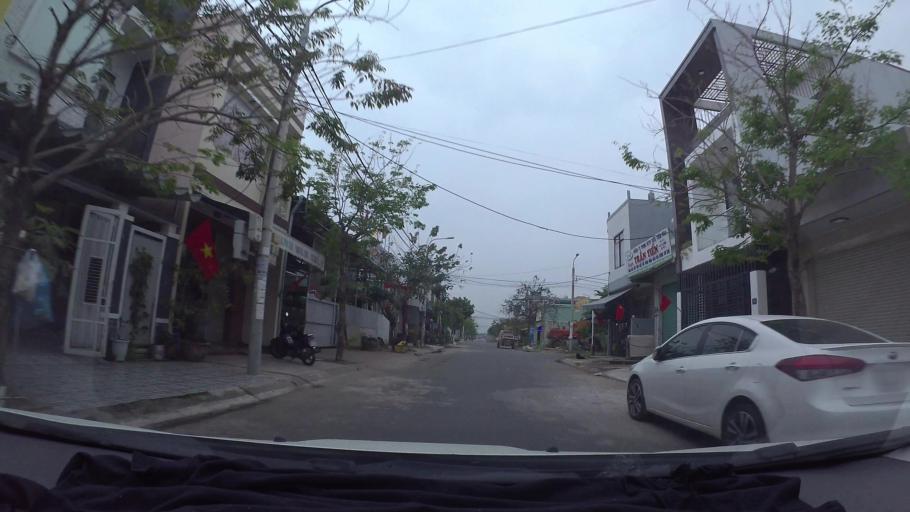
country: VN
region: Da Nang
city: Thanh Khe
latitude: 16.0453
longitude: 108.1785
